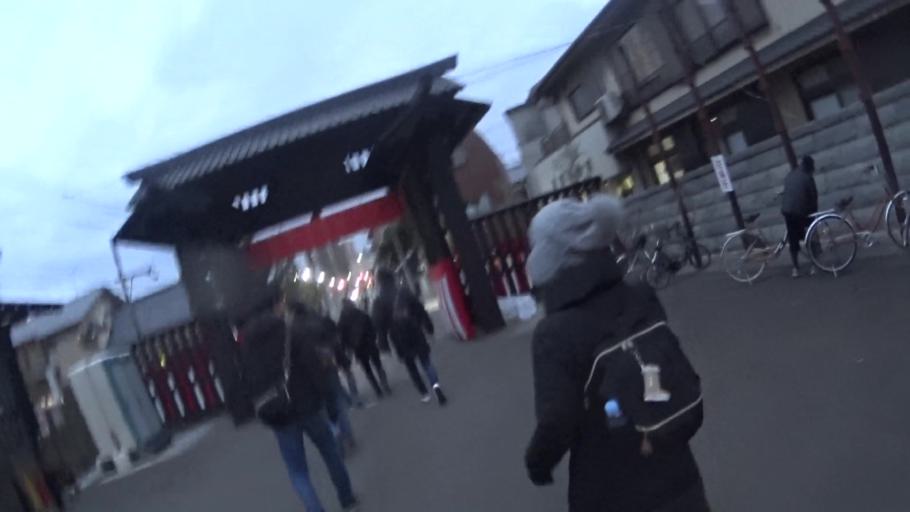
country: JP
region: Kanagawa
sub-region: Kawasaki-shi
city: Kawasaki
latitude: 35.5770
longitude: 139.7048
